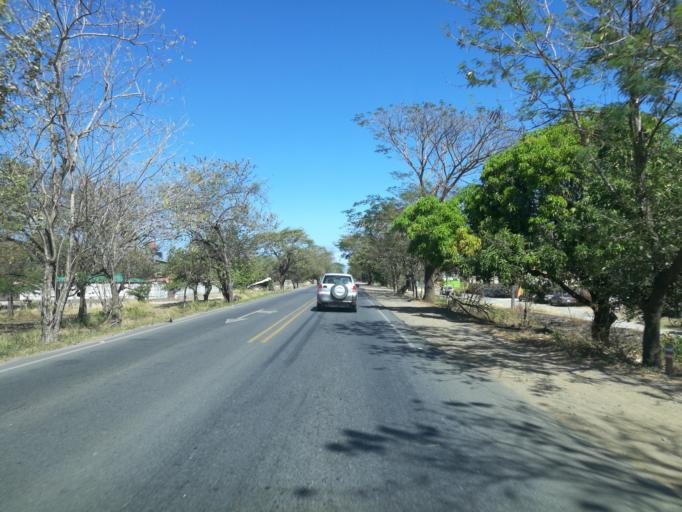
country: CR
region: Guanacaste
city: Liberia
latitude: 10.6549
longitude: -85.4667
